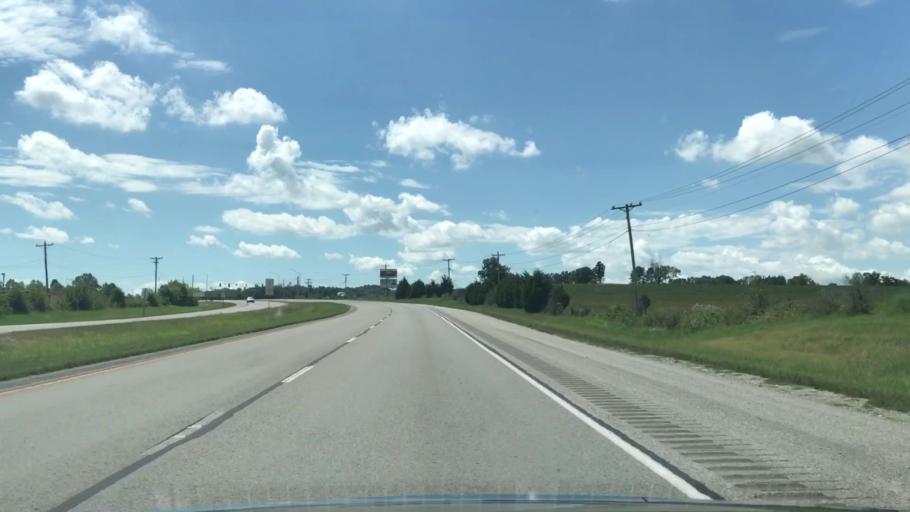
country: US
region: Kentucky
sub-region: Logan County
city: Russellville
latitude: 36.8465
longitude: -86.9196
